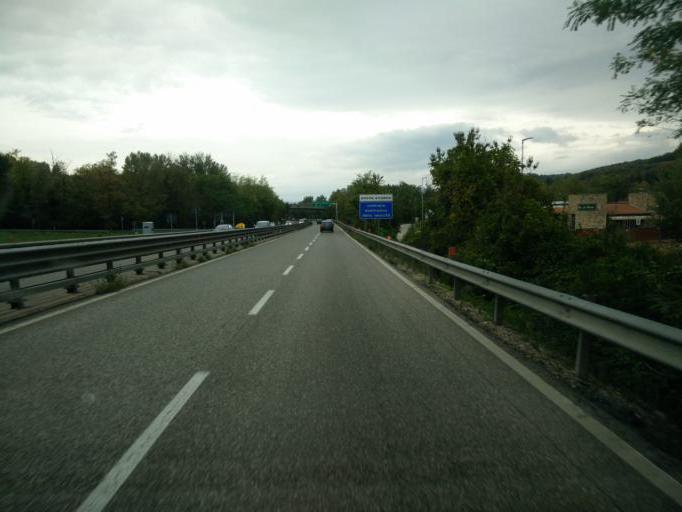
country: IT
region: Tuscany
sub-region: Province of Florence
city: Sambuca
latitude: 43.5908
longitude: 11.1999
